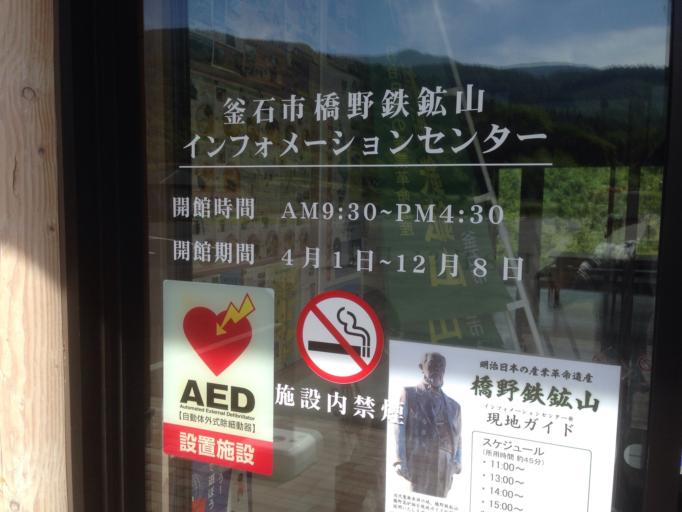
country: JP
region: Iwate
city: Tono
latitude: 39.3465
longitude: 141.6813
